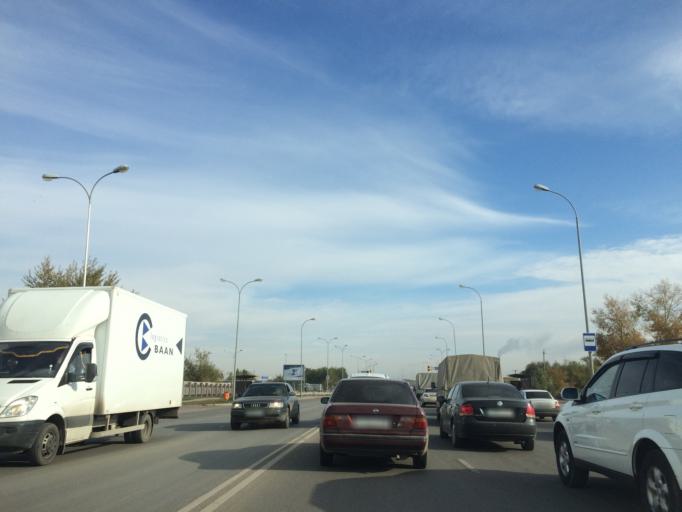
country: KZ
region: Astana Qalasy
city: Astana
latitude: 51.1673
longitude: 71.4771
